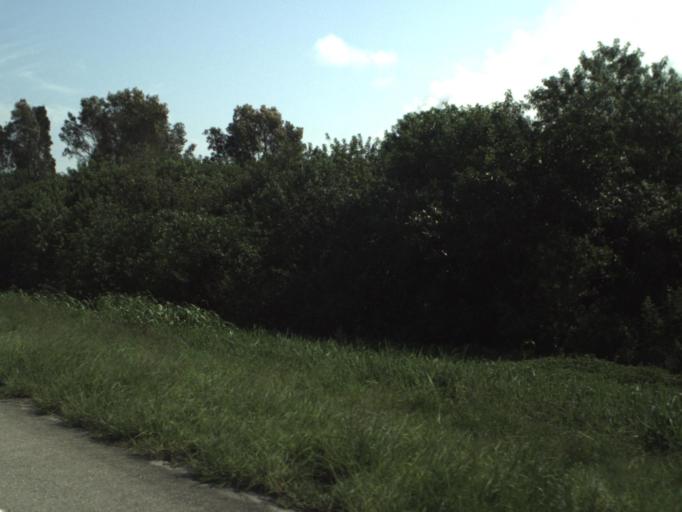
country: US
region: Florida
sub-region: Palm Beach County
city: Pahokee
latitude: 26.7722
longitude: -80.6891
